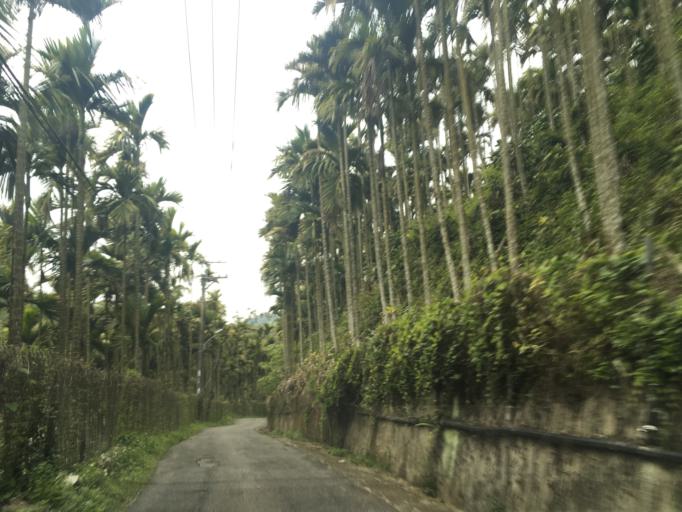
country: TW
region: Taiwan
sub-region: Taichung City
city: Taichung
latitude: 24.1514
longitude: 120.8239
